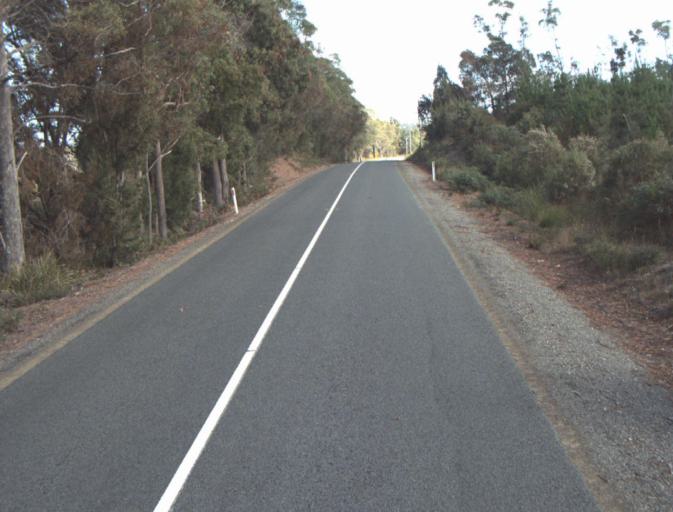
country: AU
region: Tasmania
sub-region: Dorset
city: Bridport
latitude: -41.1445
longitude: 147.2298
